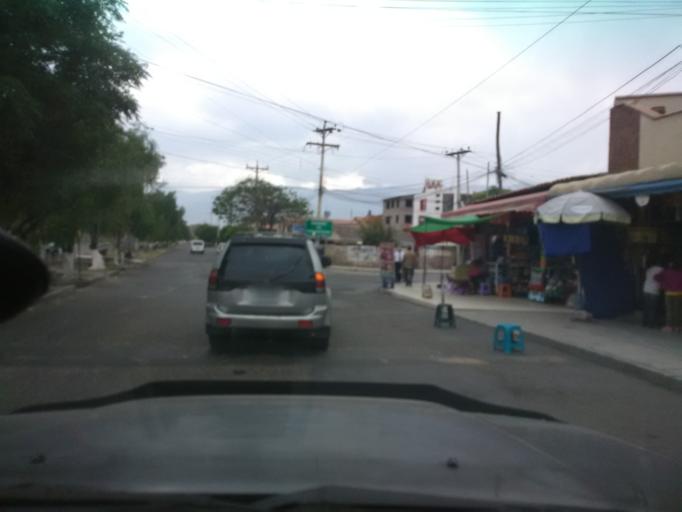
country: BO
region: Cochabamba
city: Cochabamba
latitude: -17.3815
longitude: -66.1863
